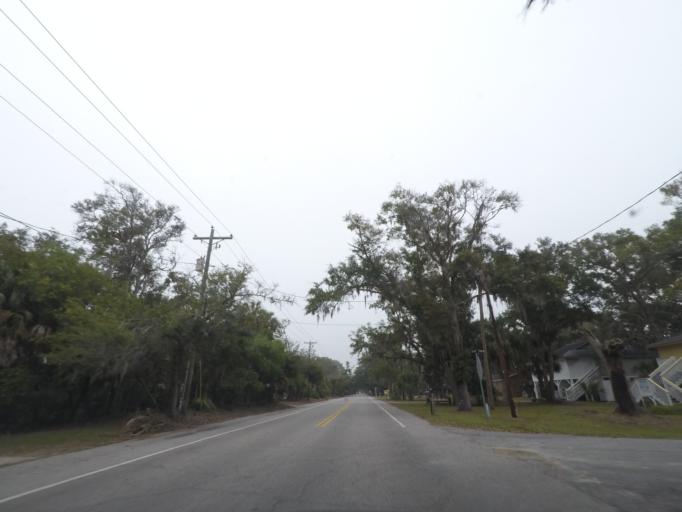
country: US
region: South Carolina
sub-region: Charleston County
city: Seabrook Island
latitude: 32.4904
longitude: -80.3210
